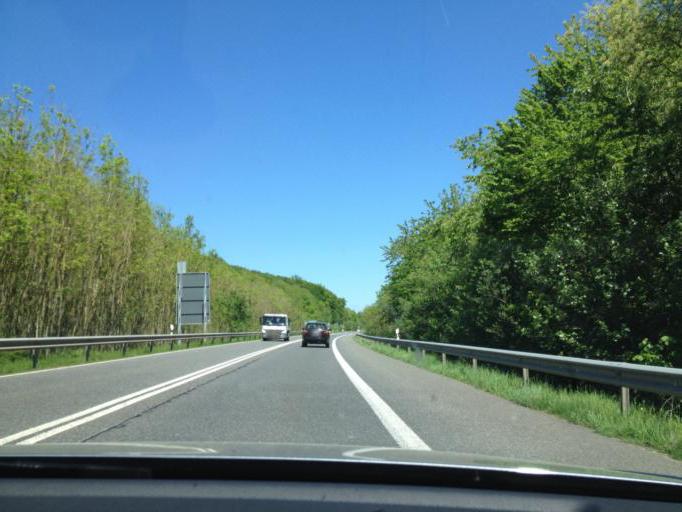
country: DE
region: Rheinland-Pfalz
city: Fliessem
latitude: 50.0296
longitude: 6.5258
